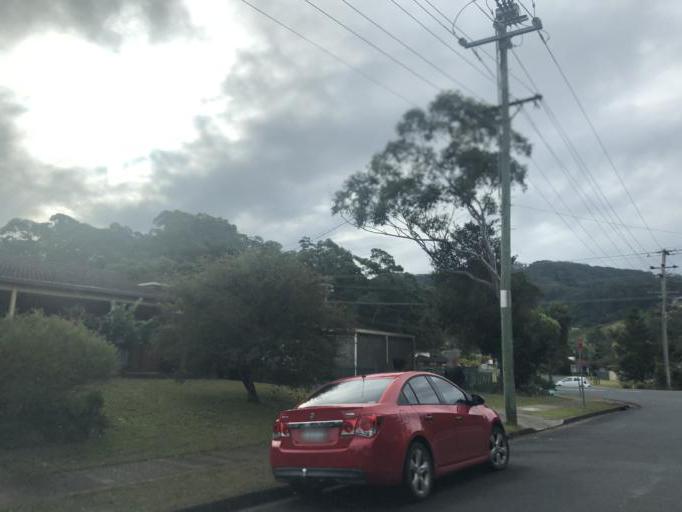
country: AU
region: New South Wales
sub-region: Coffs Harbour
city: Coffs Harbour
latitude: -30.2819
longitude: 153.1118
